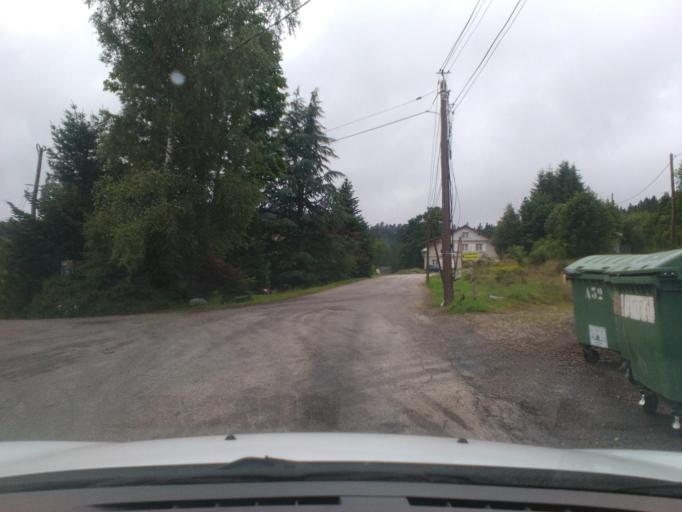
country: FR
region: Lorraine
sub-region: Departement des Vosges
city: Gerardmer
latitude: 48.0807
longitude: 6.8640
